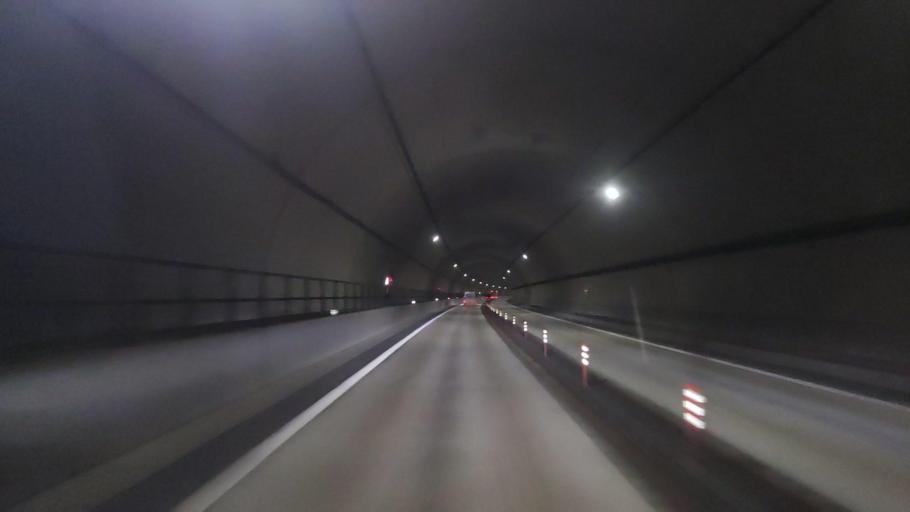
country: JP
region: Wakayama
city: Tanabe
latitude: 33.5898
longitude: 135.4411
